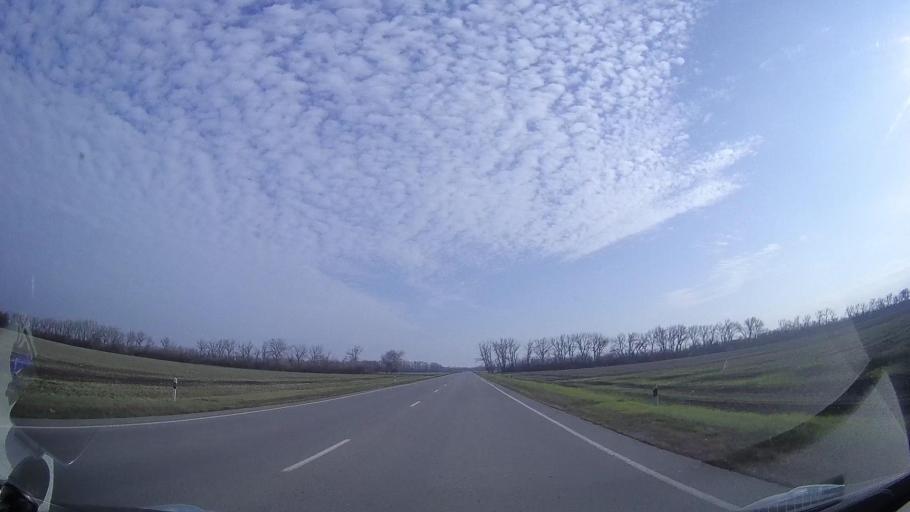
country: RU
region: Rostov
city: Tselina
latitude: 46.5227
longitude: 41.1317
